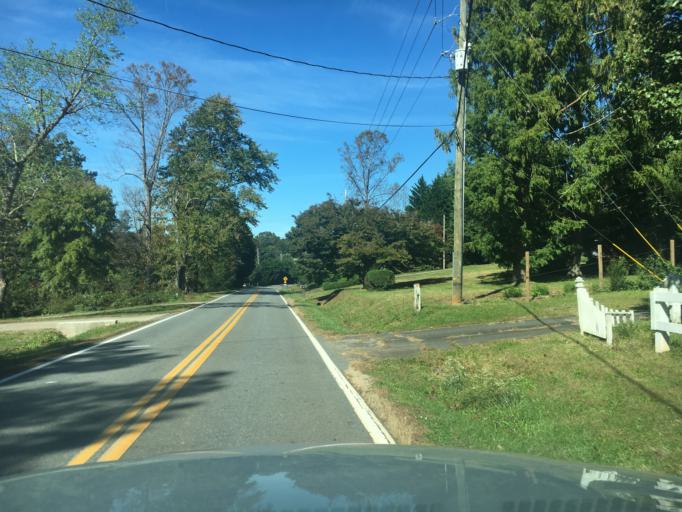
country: US
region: North Carolina
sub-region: Burke County
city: Salem
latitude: 35.6928
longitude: -81.7347
